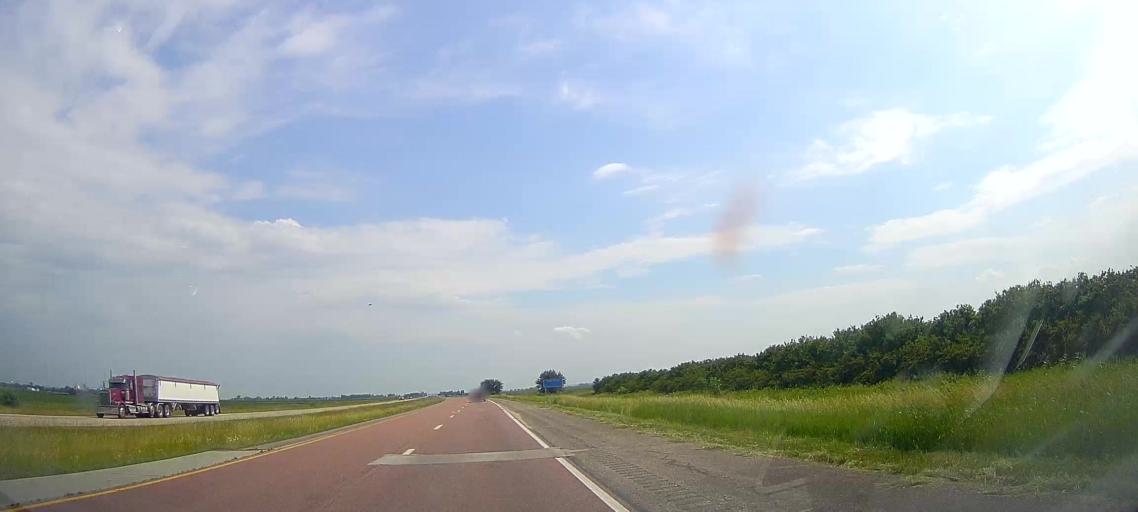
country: US
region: Iowa
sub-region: Monona County
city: Onawa
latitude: 41.9549
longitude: -96.1035
